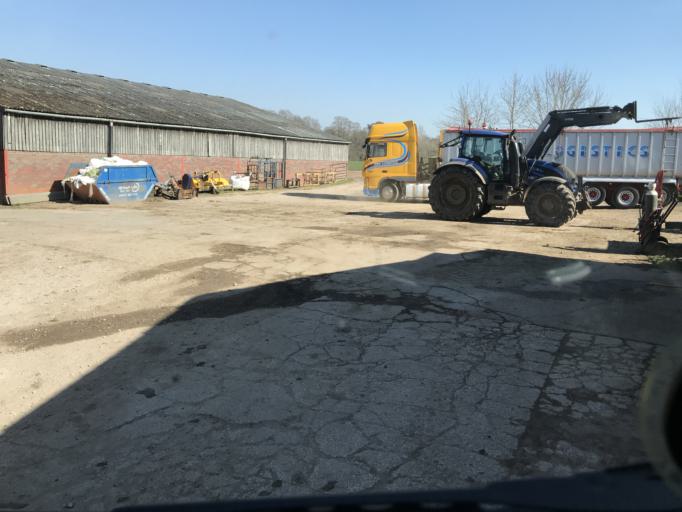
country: GB
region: England
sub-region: Cheshire East
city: Siddington
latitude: 53.2616
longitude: -2.2553
